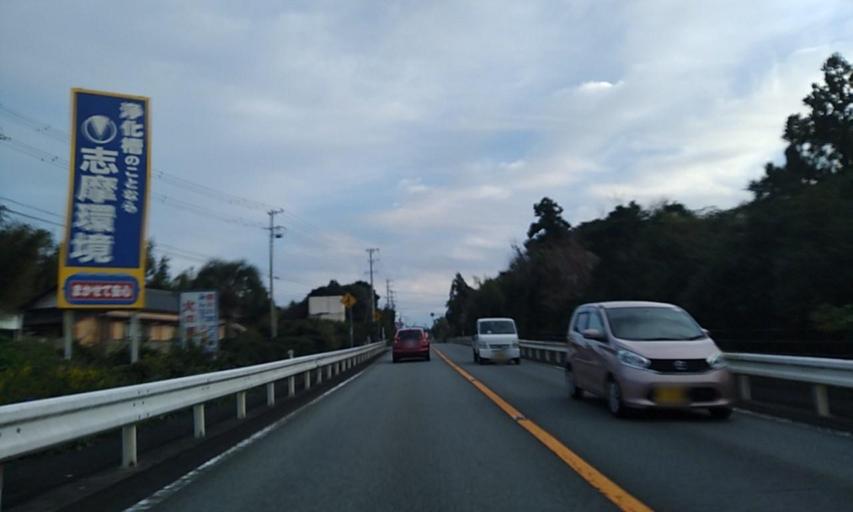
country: JP
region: Mie
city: Toba
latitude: 34.2944
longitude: 136.8805
